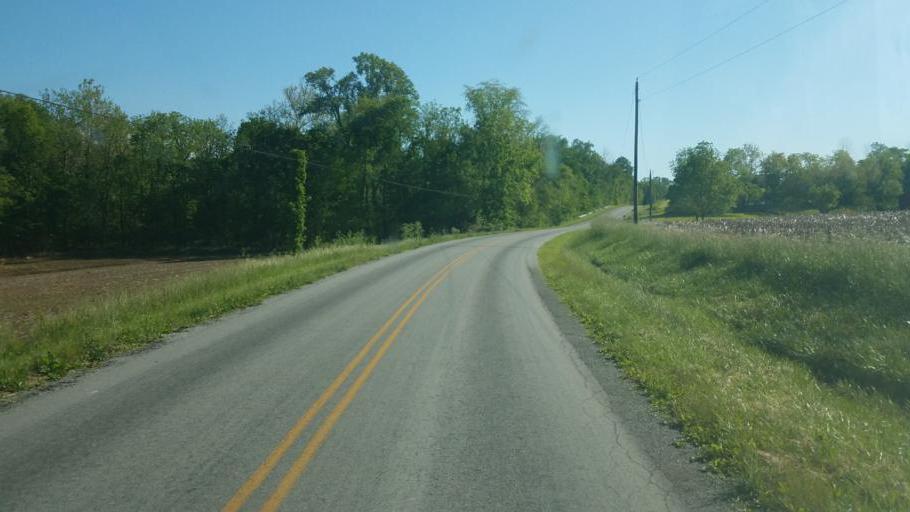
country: US
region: Ohio
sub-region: Hardin County
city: Kenton
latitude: 40.5782
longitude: -83.6307
